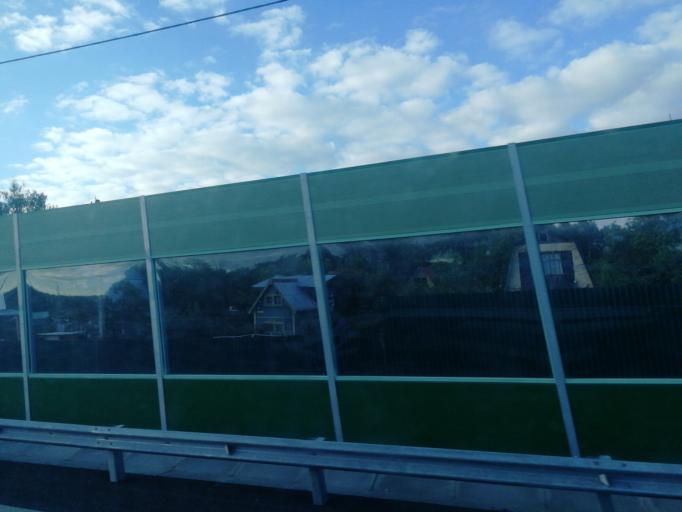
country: RU
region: Kaluga
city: Kaluga
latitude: 54.4579
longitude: 36.2782
